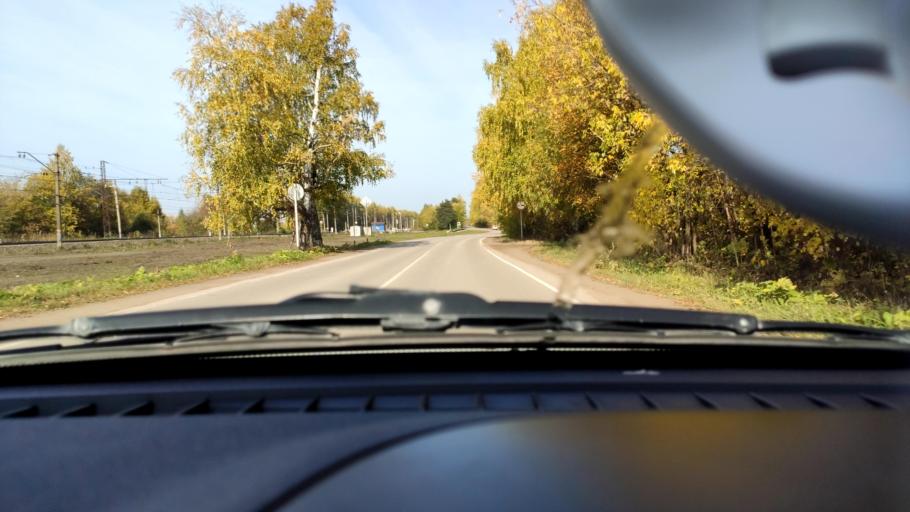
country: RU
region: Perm
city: Overyata
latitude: 58.0913
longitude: 55.8637
